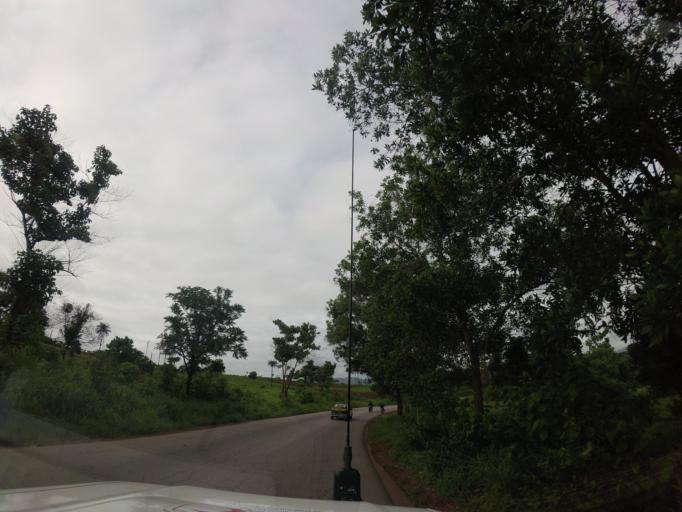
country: GN
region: Kindia
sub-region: Kindia
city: Kindia
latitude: 9.9700
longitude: -12.9350
